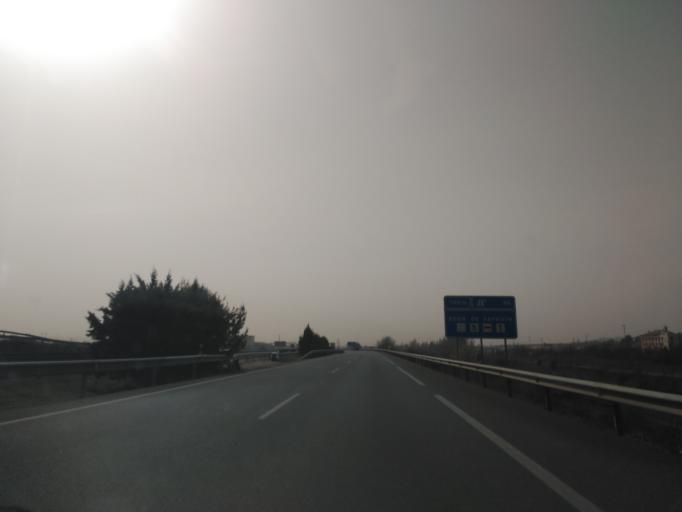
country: ES
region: Castille and Leon
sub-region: Provincia de Palencia
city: Duenas
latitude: 41.8635
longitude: -4.5466
